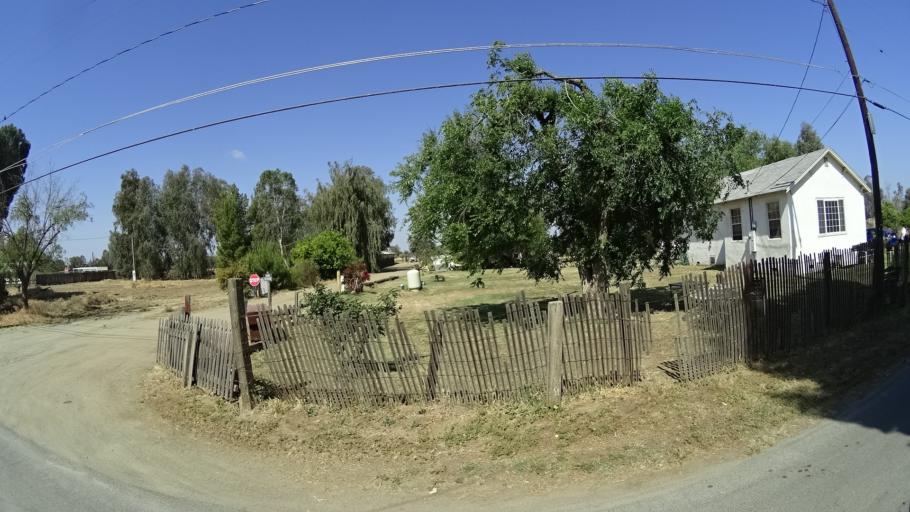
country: US
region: California
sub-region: Kings County
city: Home Garden
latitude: 36.3086
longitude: -119.6302
